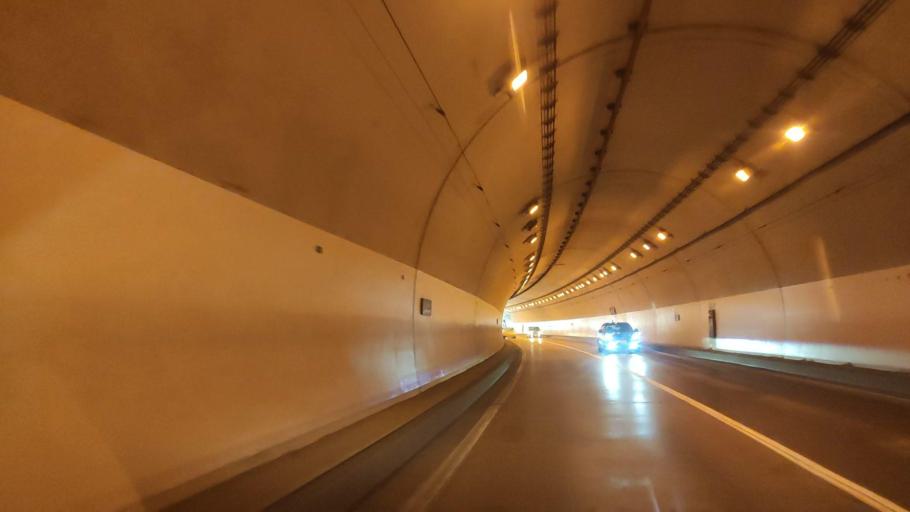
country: JP
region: Hokkaido
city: Rumoi
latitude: 43.6746
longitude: 141.3468
